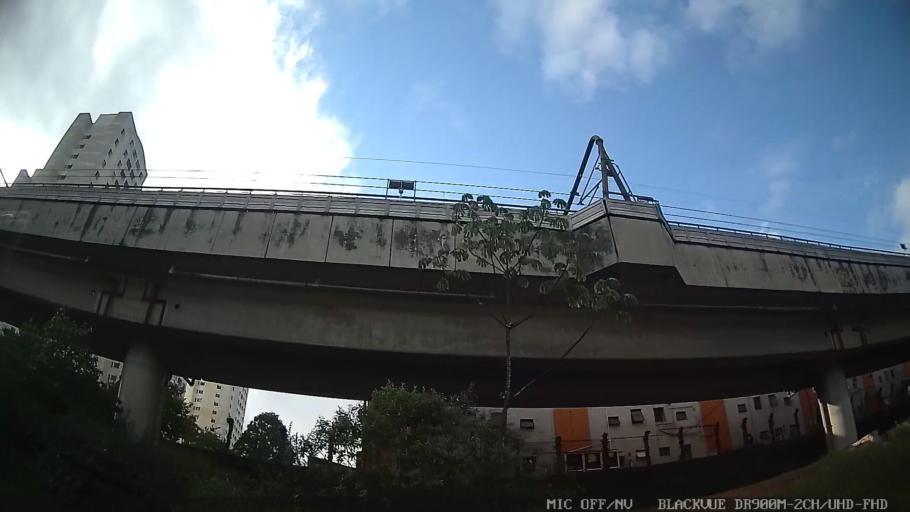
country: BR
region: Sao Paulo
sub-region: Taboao Da Serra
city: Taboao da Serra
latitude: -23.6467
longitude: -46.7572
